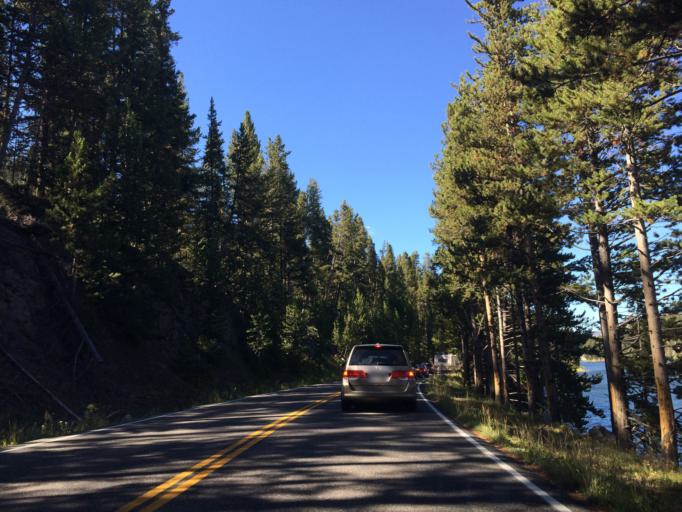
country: US
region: Montana
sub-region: Gallatin County
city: West Yellowstone
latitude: 44.6854
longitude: -110.4965
